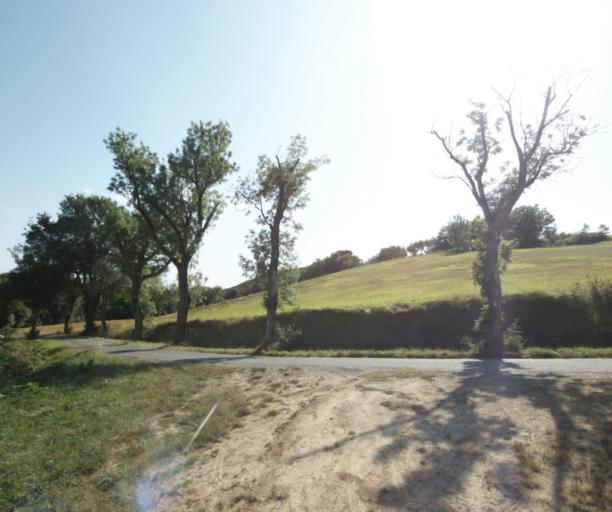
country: FR
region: Midi-Pyrenees
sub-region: Departement de la Haute-Garonne
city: Avignonet-Lauragais
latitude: 43.4186
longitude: 1.8250
